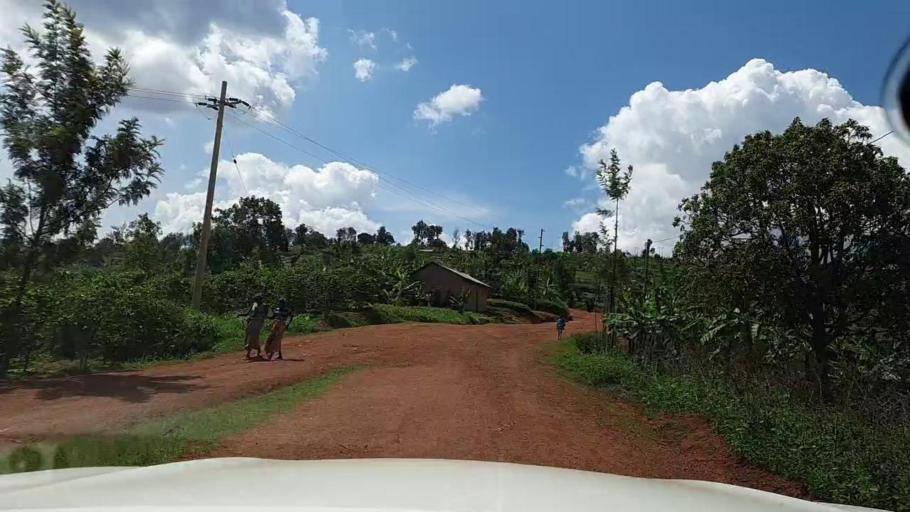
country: RW
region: Southern Province
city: Butare
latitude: -2.7449
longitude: 29.7024
